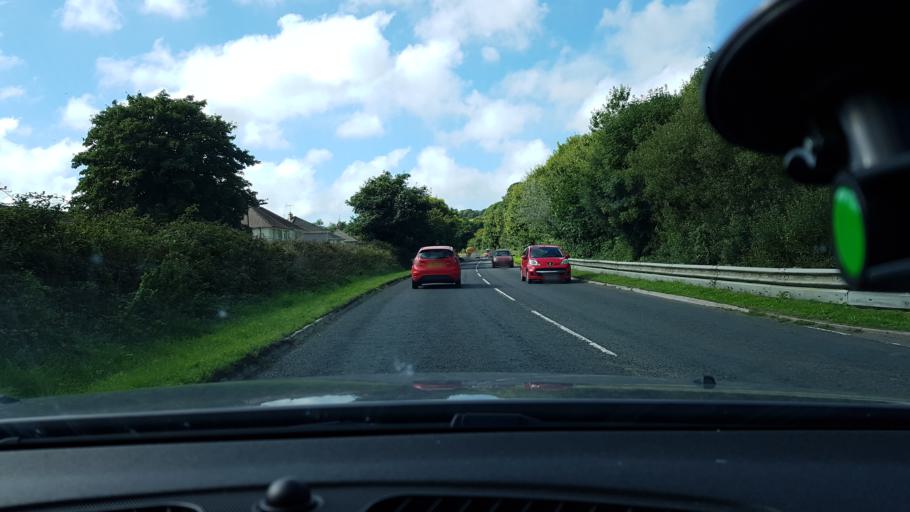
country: GB
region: England
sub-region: Cornwall
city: Penzance
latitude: 50.1281
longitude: -5.5367
